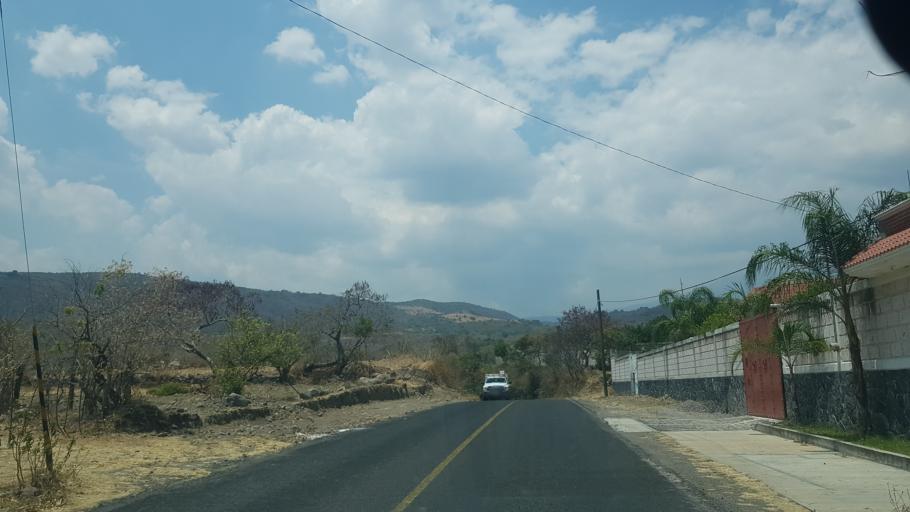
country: MX
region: Puebla
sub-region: Atzitzihuacan
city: Santiago Atzitzihuacan
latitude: 18.8415
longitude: -98.5847
